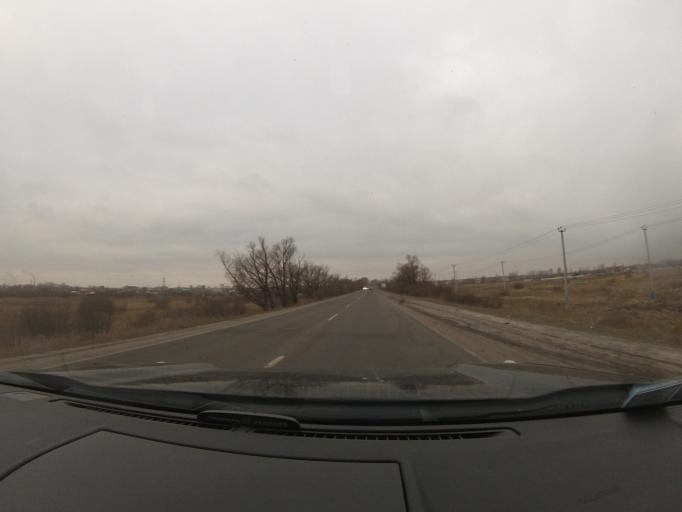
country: RU
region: Moskovskaya
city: Lopatinskiy
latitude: 55.3270
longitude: 38.7301
